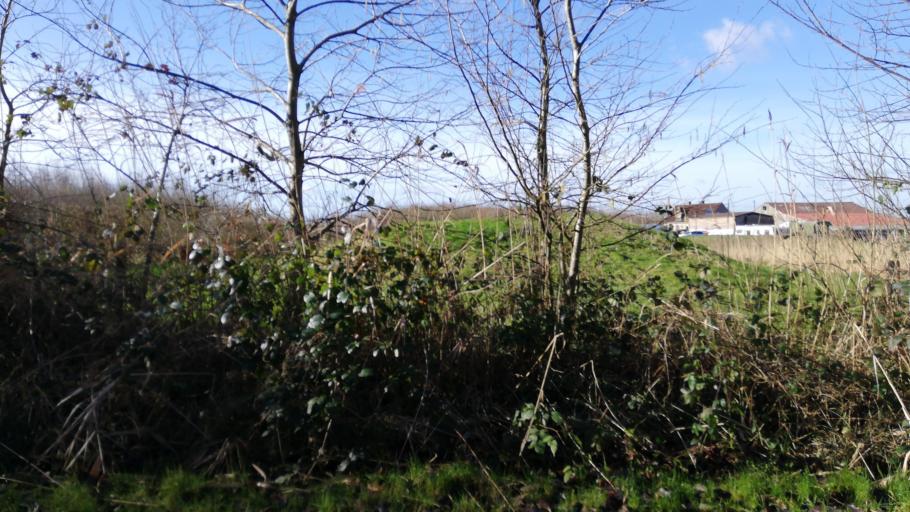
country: BE
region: Flanders
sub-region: Provincie West-Vlaanderen
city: Poperinge
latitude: 50.8912
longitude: 2.6979
